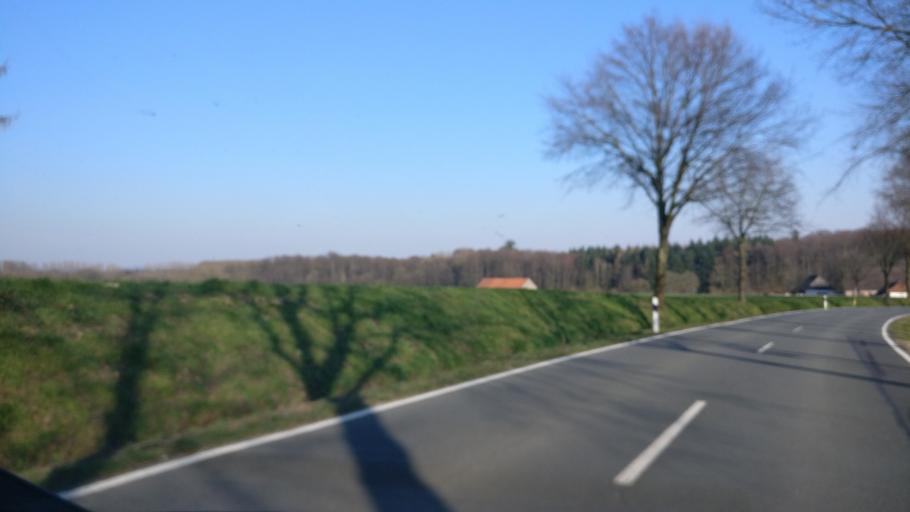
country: DE
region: North Rhine-Westphalia
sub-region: Regierungsbezirk Detmold
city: Lage
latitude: 52.0069
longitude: 8.7489
